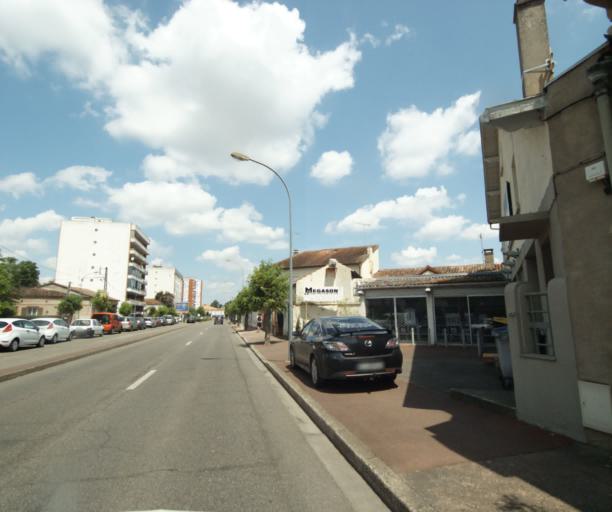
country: FR
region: Midi-Pyrenees
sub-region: Departement du Tarn-et-Garonne
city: Montauban
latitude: 44.0194
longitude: 1.3628
